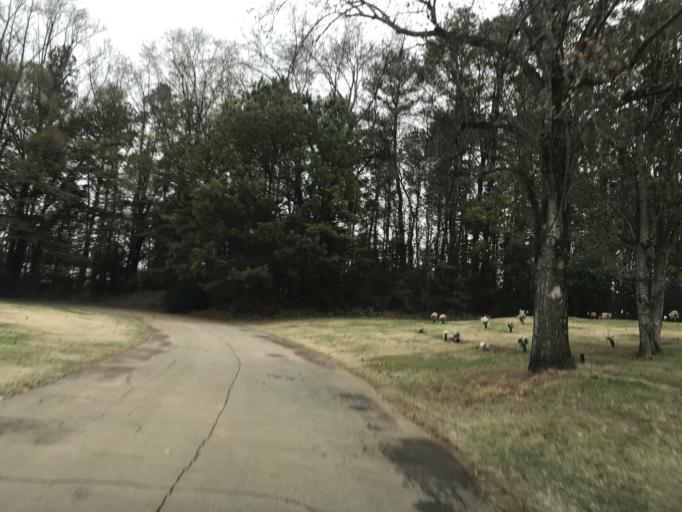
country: US
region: Georgia
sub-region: DeKalb County
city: Clarkston
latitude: 33.8335
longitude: -84.2495
